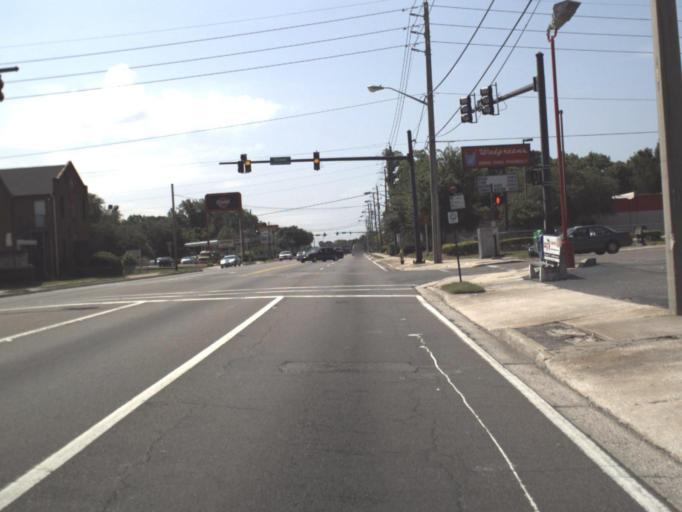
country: US
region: Florida
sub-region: Duval County
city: Jacksonville
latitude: 30.3888
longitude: -81.6780
